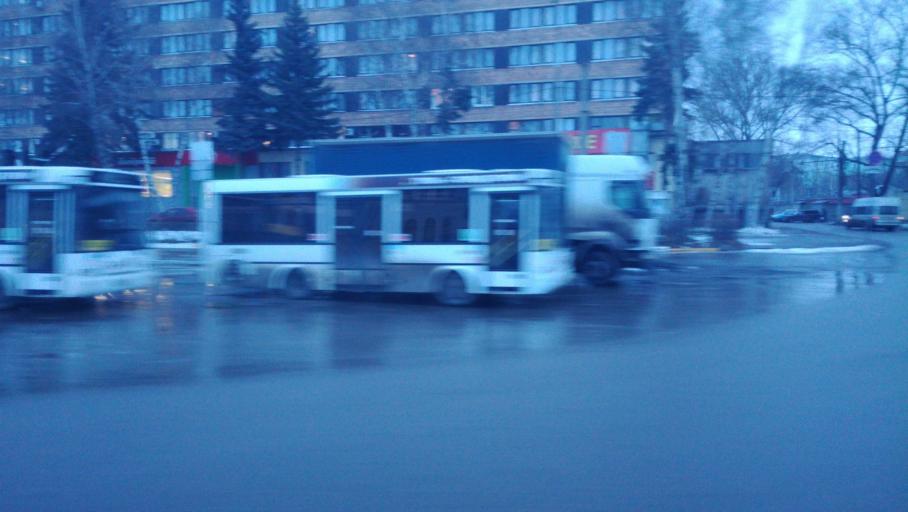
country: RU
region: Tula
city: Tula
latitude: 54.1983
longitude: 37.5780
